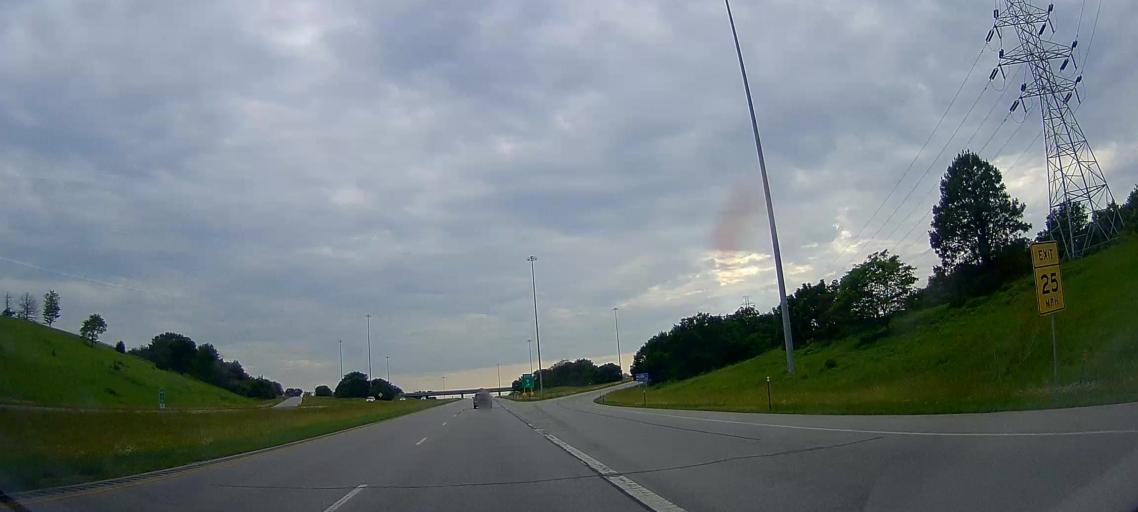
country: US
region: Iowa
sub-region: Pottawattamie County
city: Carter Lake
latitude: 41.3430
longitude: -96.0192
